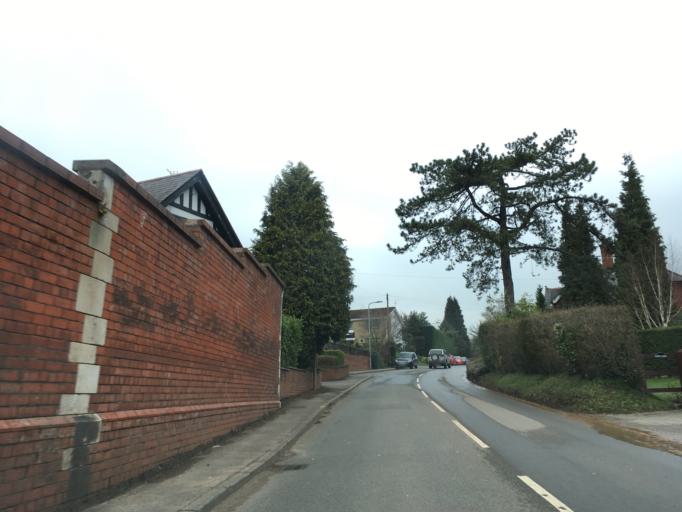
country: GB
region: Wales
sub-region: Cardiff
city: Cardiff
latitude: 51.5383
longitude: -3.1696
